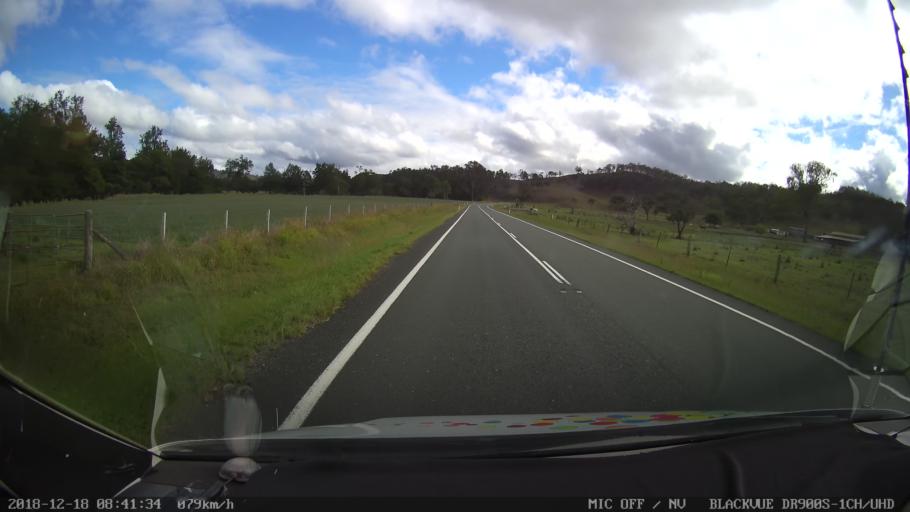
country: AU
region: Queensland
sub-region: Logan
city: Cedar Vale
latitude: -28.2351
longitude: 152.8579
